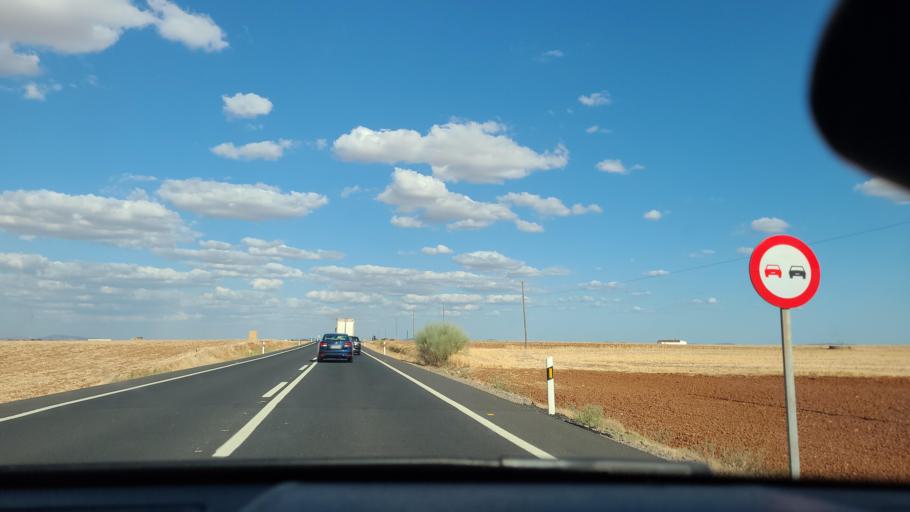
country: ES
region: Extremadura
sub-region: Provincia de Badajoz
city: Berlanga
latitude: 38.2654
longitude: -5.7570
